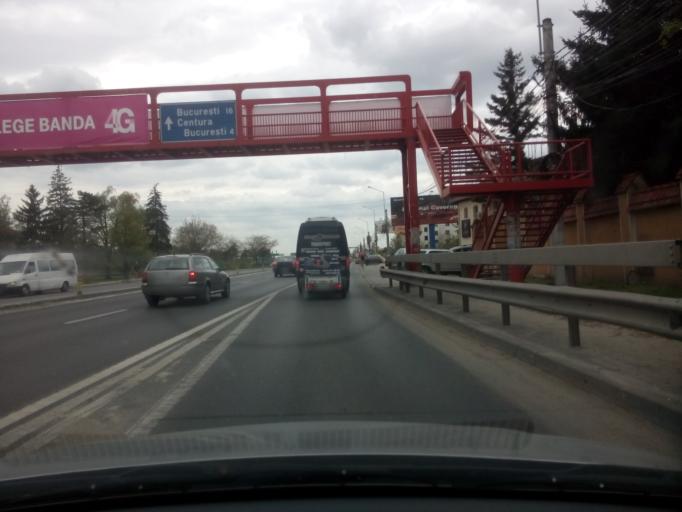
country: RO
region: Ilfov
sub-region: Comuna Otopeni
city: Otopeni
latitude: 44.5698
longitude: 26.0697
